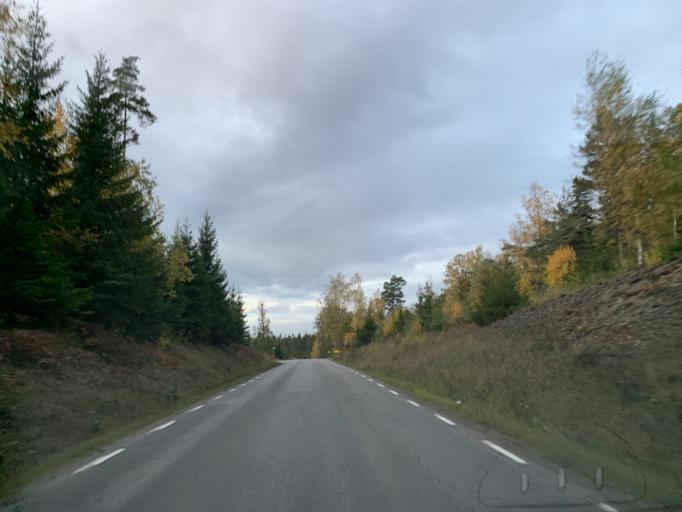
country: SE
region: Stockholm
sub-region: Nynashamns Kommun
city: Osmo
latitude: 58.9358
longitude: 17.7604
